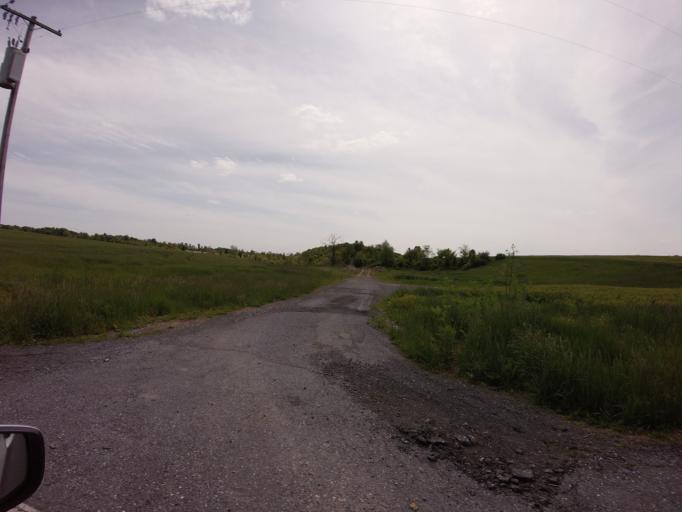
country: US
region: Maryland
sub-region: Frederick County
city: Woodsboro
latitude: 39.5330
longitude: -77.2919
